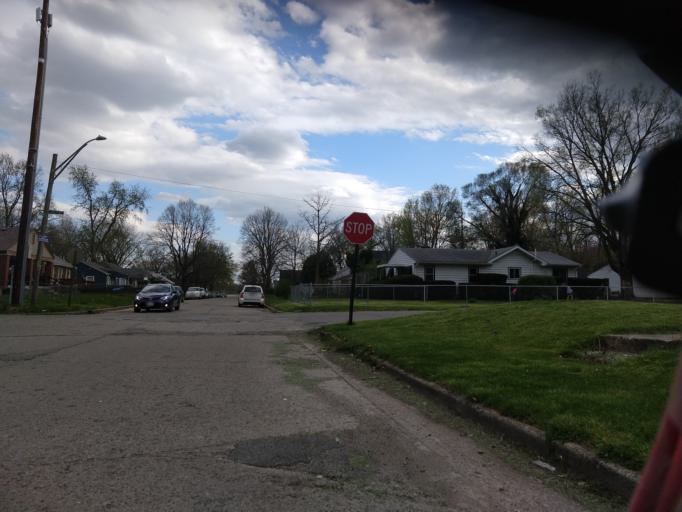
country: US
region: Indiana
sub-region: Marion County
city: Broad Ripple
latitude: 39.8350
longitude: -86.1277
